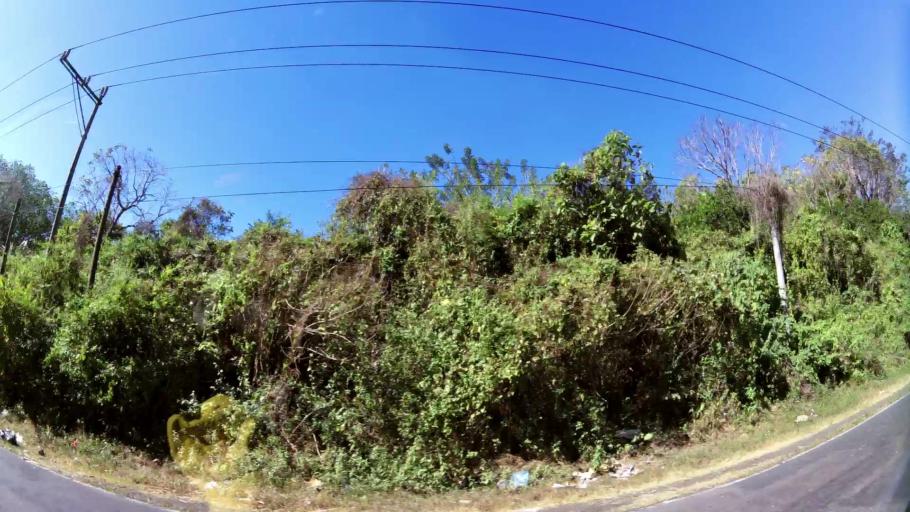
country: SV
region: La Libertad
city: San Juan Opico
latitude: 13.8329
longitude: -89.3584
